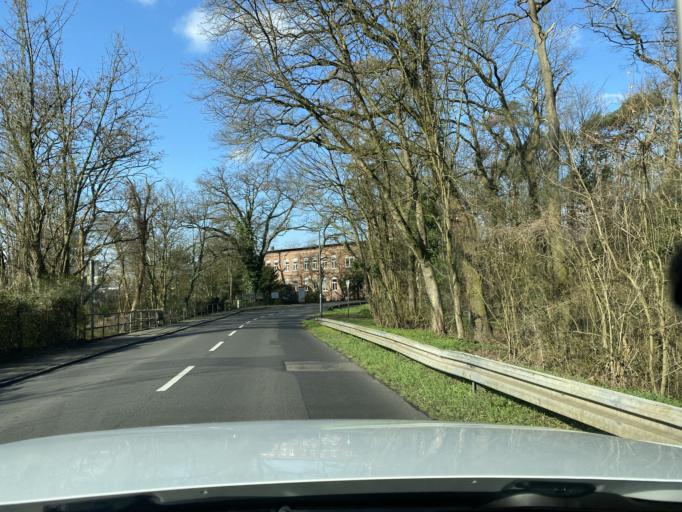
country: DE
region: North Rhine-Westphalia
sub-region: Regierungsbezirk Koln
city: Merheim
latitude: 50.9831
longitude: 7.0769
